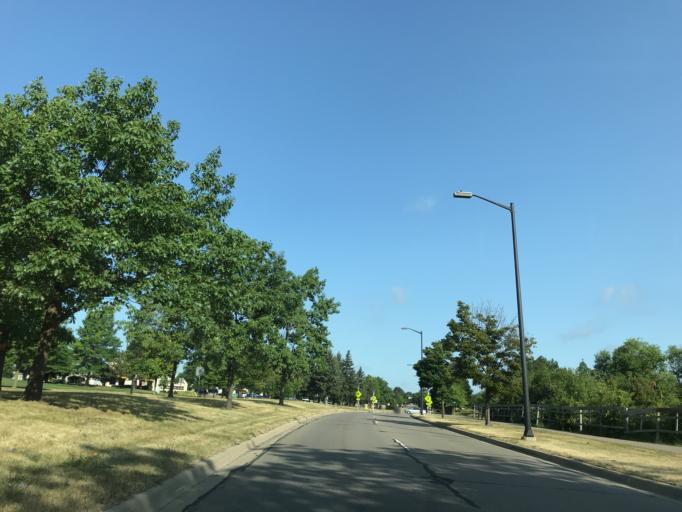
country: US
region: Michigan
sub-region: Washtenaw County
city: Ann Arbor
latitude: 42.2442
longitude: -83.7553
